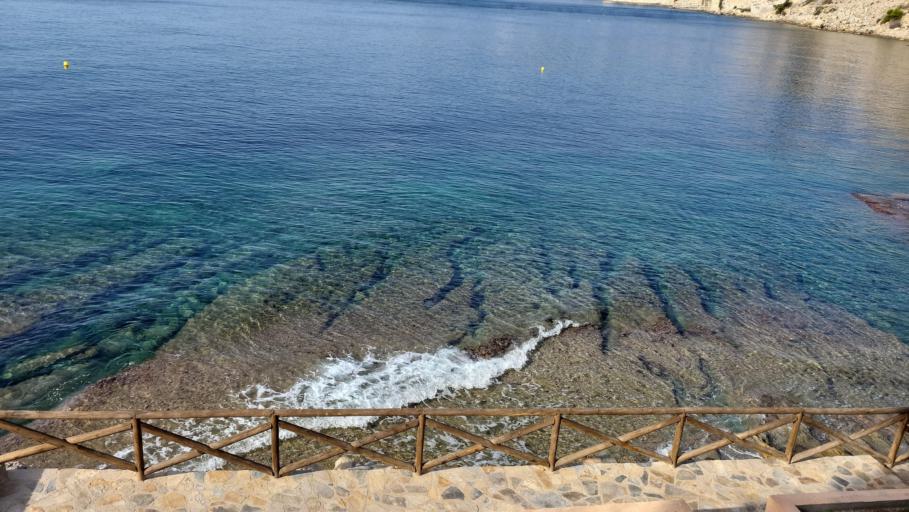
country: ES
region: Valencia
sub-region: Provincia de Alicante
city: Moraira
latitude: 38.6741
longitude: 0.1137
